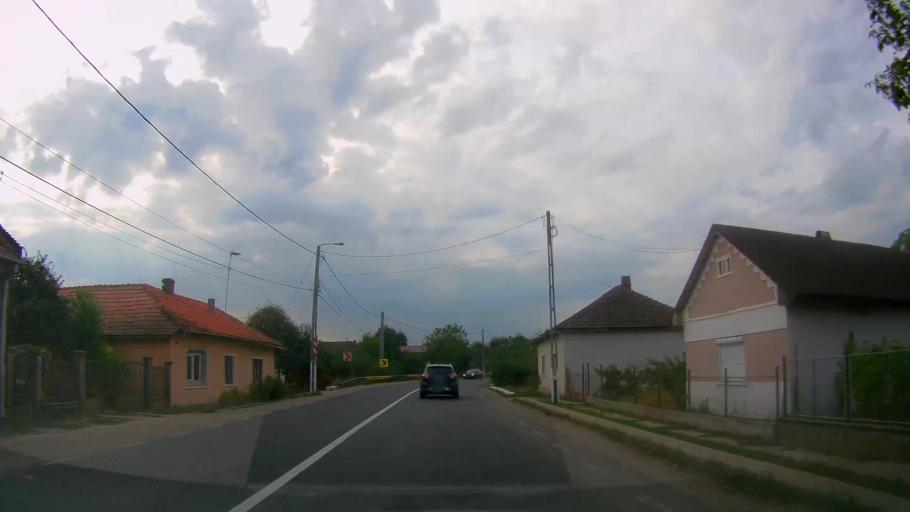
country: RO
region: Satu Mare
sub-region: Oras Ardud
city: Ardud
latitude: 47.5863
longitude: 22.8852
